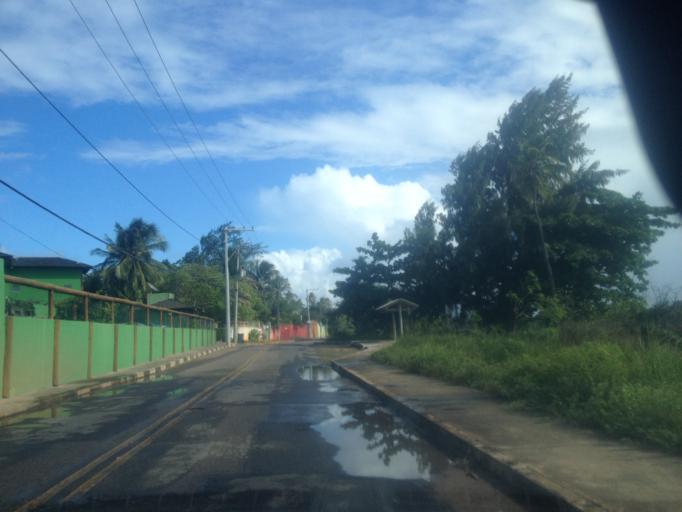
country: BR
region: Bahia
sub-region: Mata De Sao Joao
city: Mata de Sao Joao
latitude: -12.6067
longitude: -38.0405
